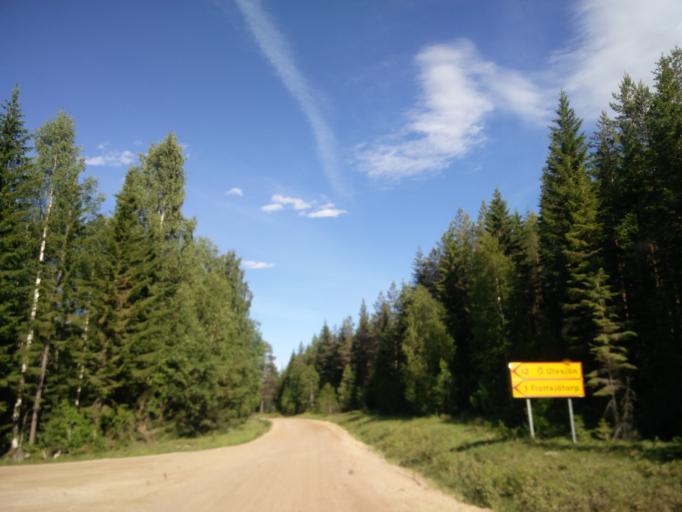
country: SE
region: Gaevleborg
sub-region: Hudiksvalls Kommun
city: Delsbo
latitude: 62.1867
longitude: 16.4542
